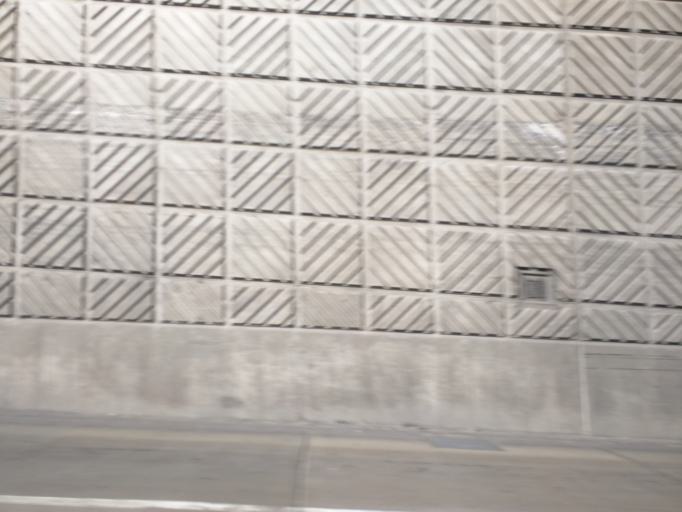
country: US
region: New York
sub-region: Queens County
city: Jamaica
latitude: 40.7120
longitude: -73.8227
